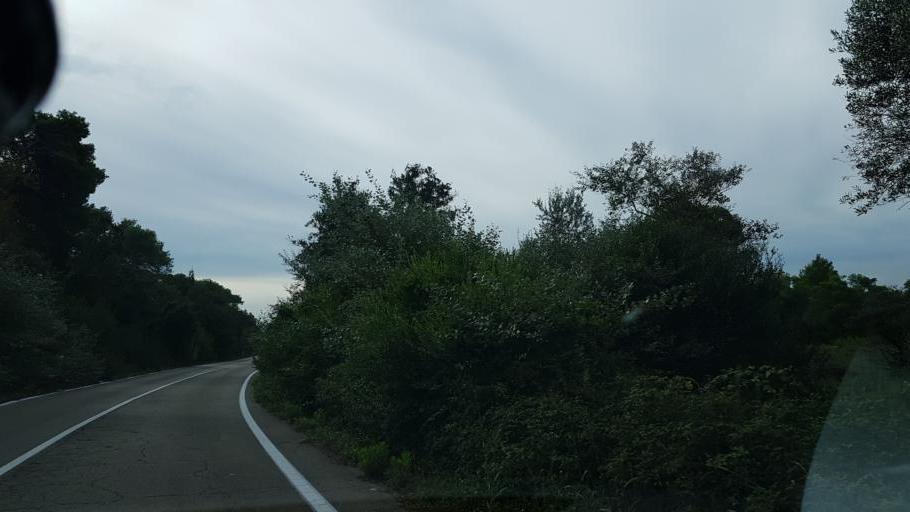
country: IT
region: Apulia
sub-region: Provincia di Lecce
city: Struda
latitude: 40.3816
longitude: 18.3009
